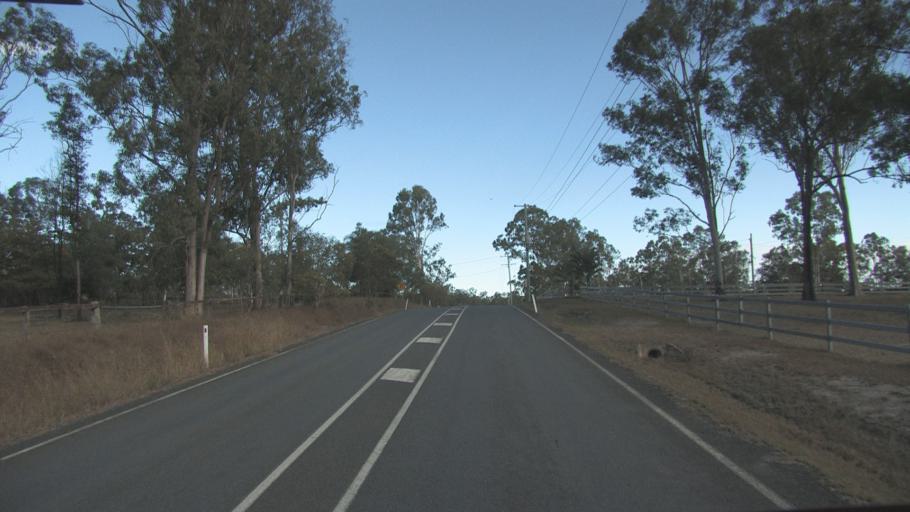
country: AU
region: Queensland
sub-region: Logan
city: Cedar Vale
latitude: -27.8304
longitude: 153.0530
